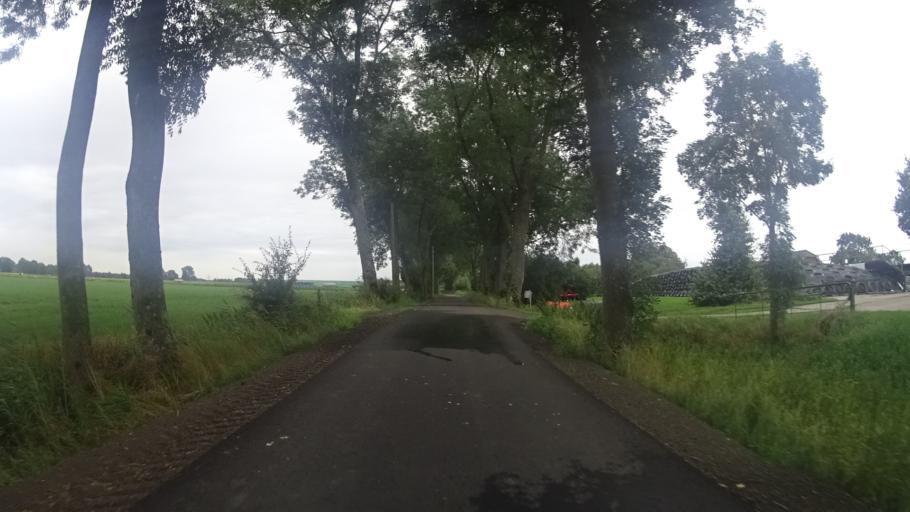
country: DE
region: Schleswig-Holstein
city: Sommerland
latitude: 53.7825
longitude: 9.5477
